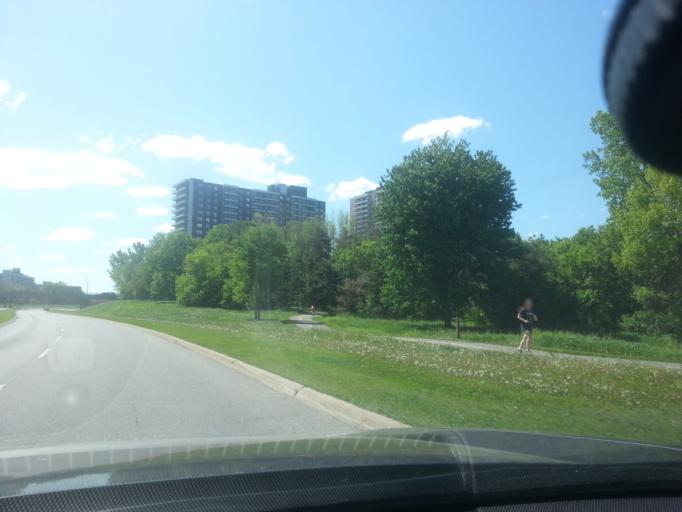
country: CA
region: Ontario
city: Bells Corners
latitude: 45.3715
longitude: -75.7854
